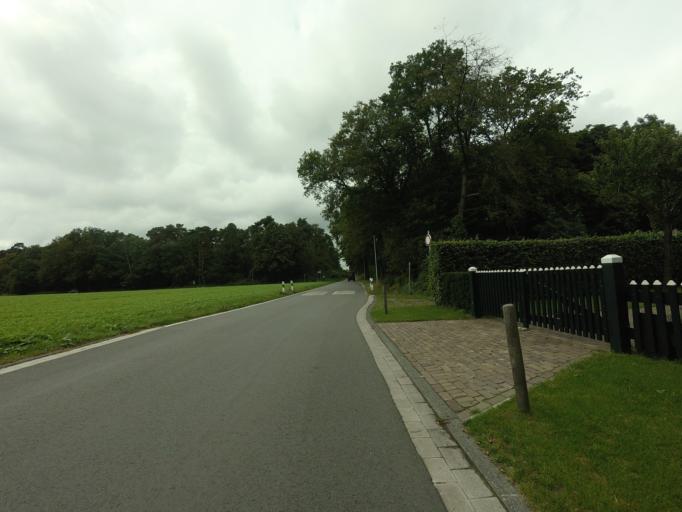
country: NL
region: Overijssel
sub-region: Gemeente Losser
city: Losser
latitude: 52.2648
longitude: 7.0495
